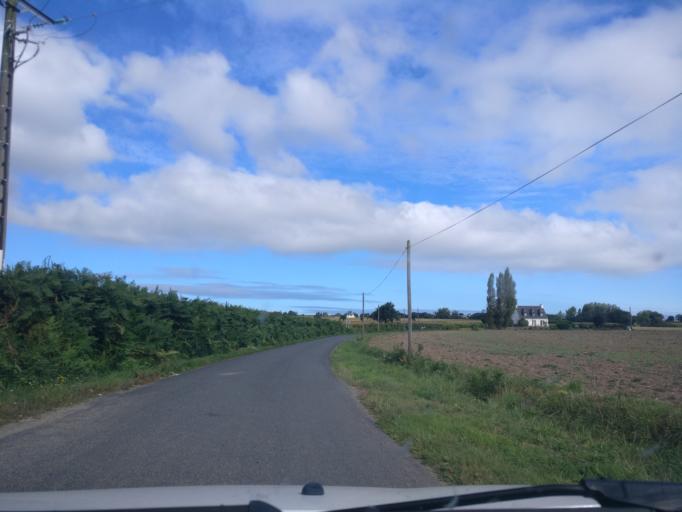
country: FR
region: Brittany
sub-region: Departement des Cotes-d'Armor
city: Rospez
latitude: 48.7461
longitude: -3.3741
